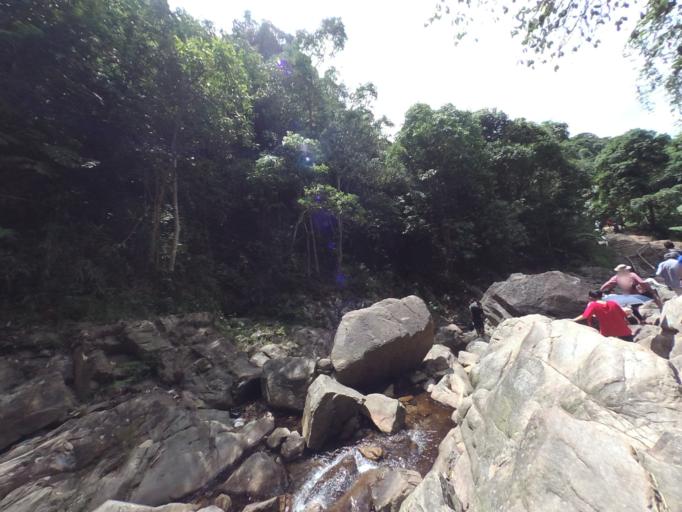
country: VN
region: Thua Thien-Hue
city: A Luoi
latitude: 16.3090
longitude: 107.2171
